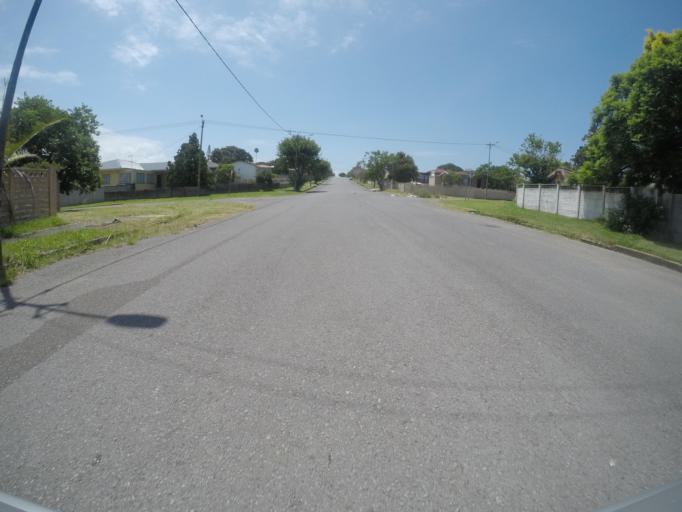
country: ZA
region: Eastern Cape
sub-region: Buffalo City Metropolitan Municipality
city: East London
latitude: -32.9780
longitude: 27.8797
